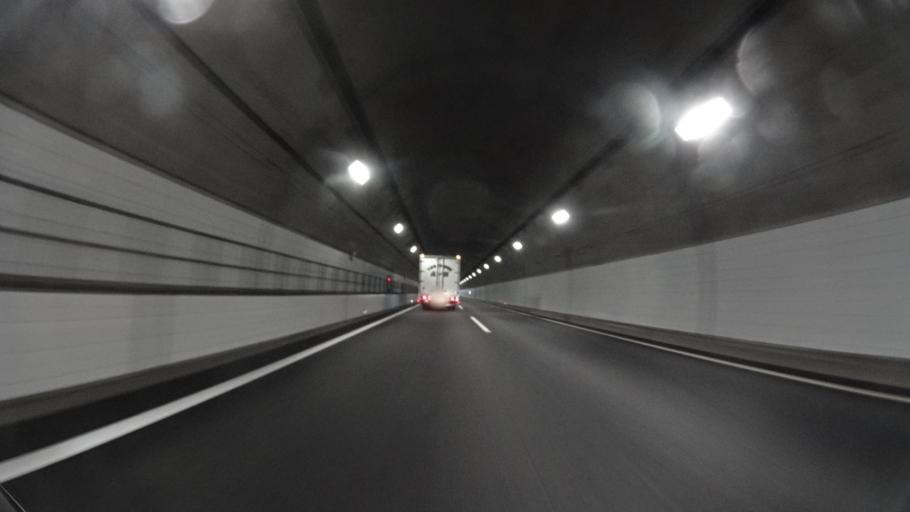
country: JP
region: Tochigi
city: Tanuma
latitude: 36.3503
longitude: 139.6107
